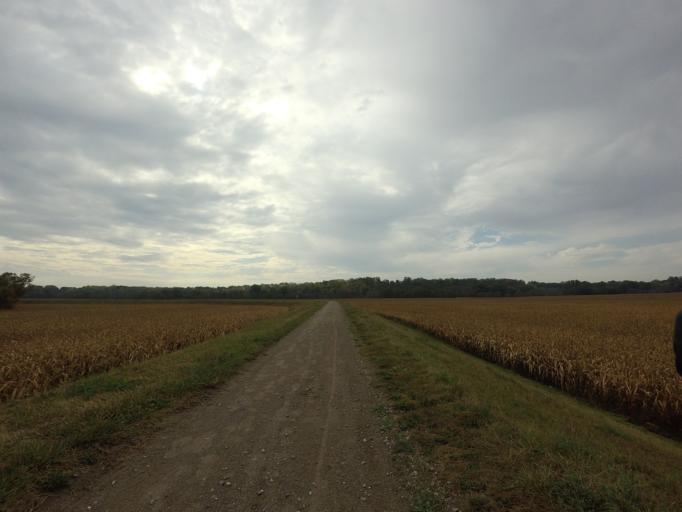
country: CA
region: Ontario
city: Brantford
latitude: 43.1155
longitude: -80.2552
